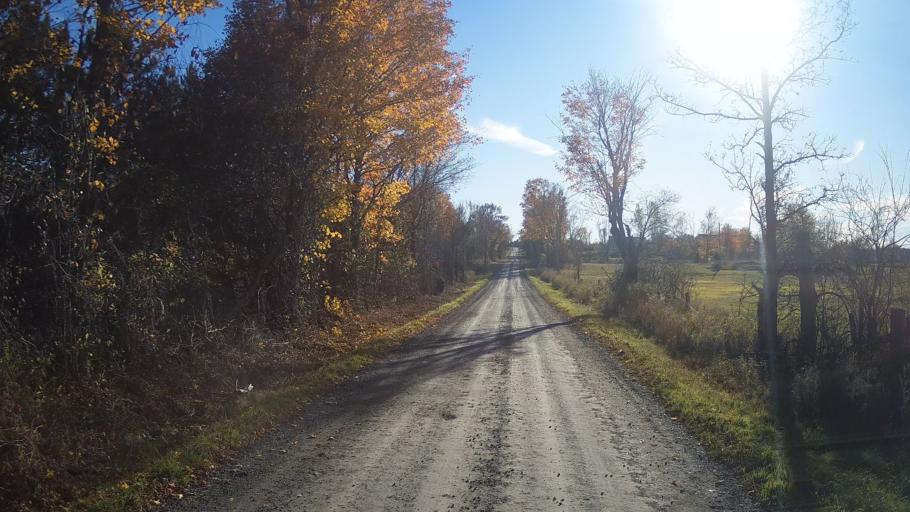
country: CA
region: Ontario
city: Perth
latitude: 44.7105
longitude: -76.4227
